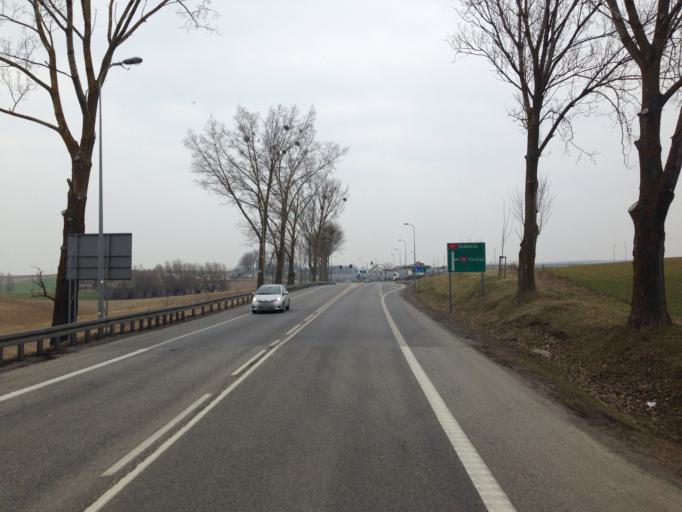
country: PL
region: Pomeranian Voivodeship
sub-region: Powiat tczewski
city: Gniew
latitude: 53.7711
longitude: 18.7695
